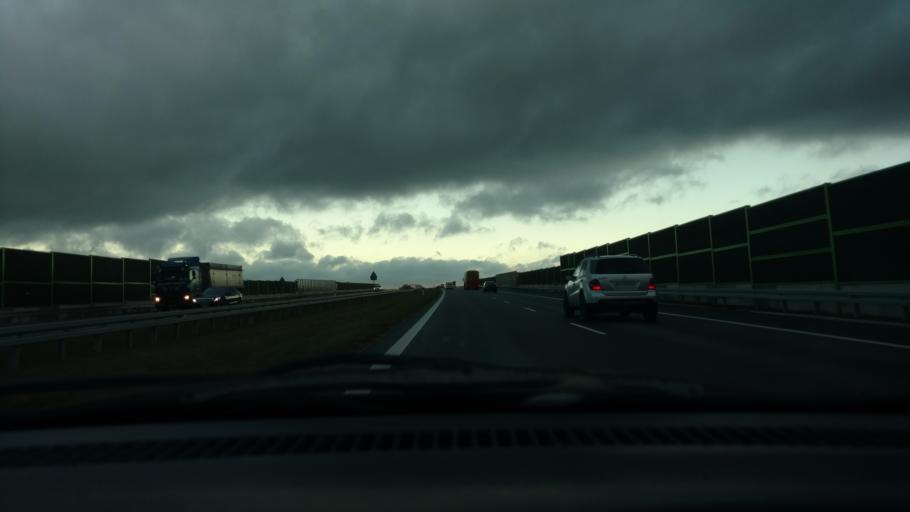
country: PL
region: Lodz Voivodeship
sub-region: Powiat lodzki wschodni
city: Andrespol
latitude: 51.7248
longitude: 19.6070
